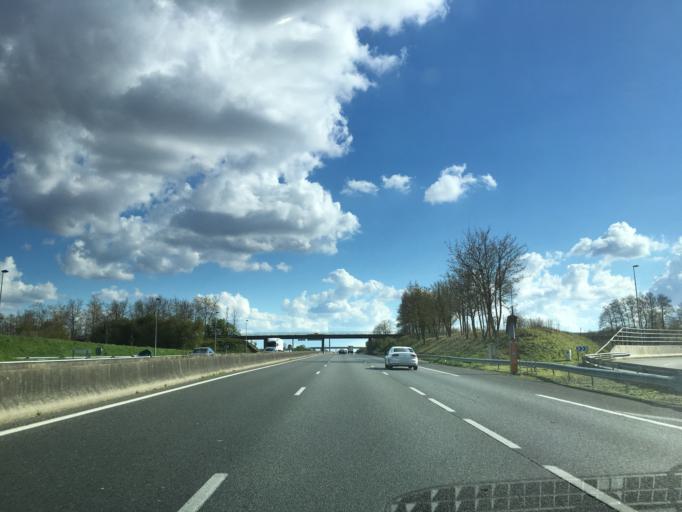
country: FR
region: Nord-Pas-de-Calais
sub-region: Departement du Pas-de-Calais
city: Bapaume
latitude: 50.1032
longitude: 2.8714
